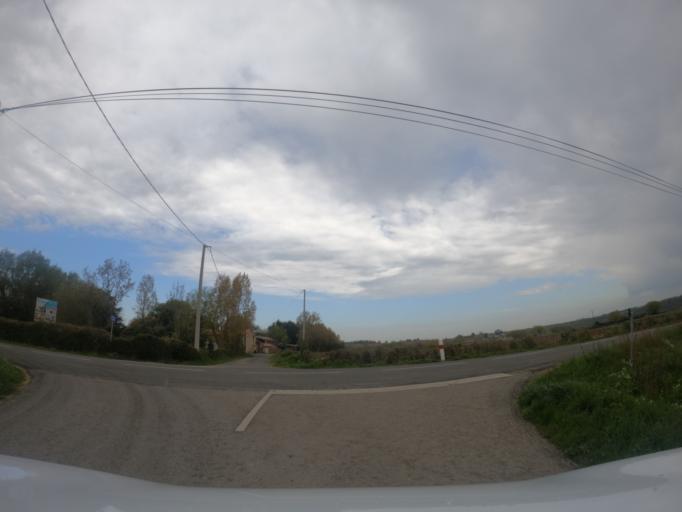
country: FR
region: Pays de la Loire
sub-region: Departement de la Vendee
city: Le Champ-Saint-Pere
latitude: 46.5237
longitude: -1.3292
